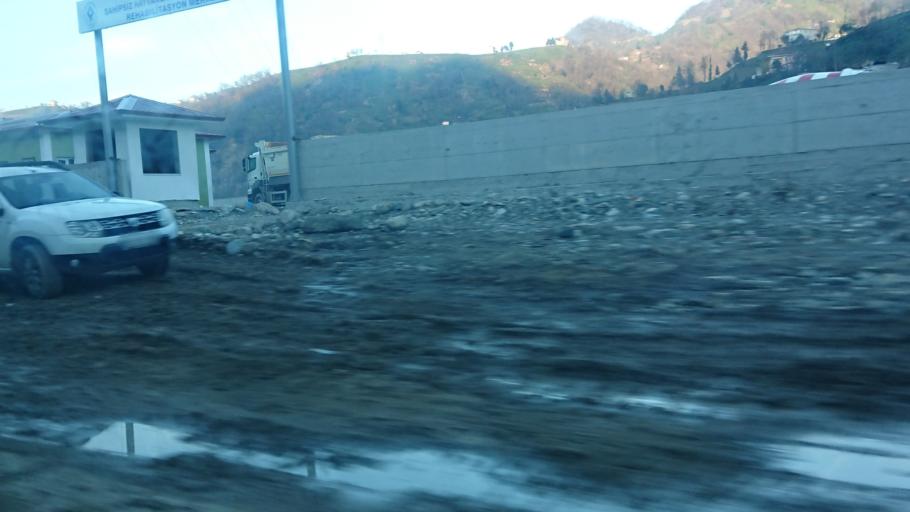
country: TR
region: Rize
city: Gundogdu
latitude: 41.0234
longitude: 40.5767
